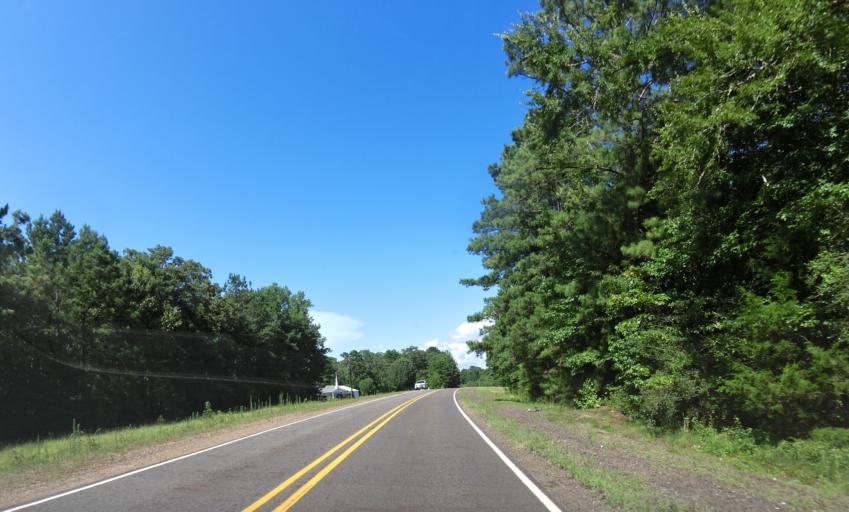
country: US
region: Louisiana
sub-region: Sabine Parish
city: Many
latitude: 31.2787
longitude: -93.5477
